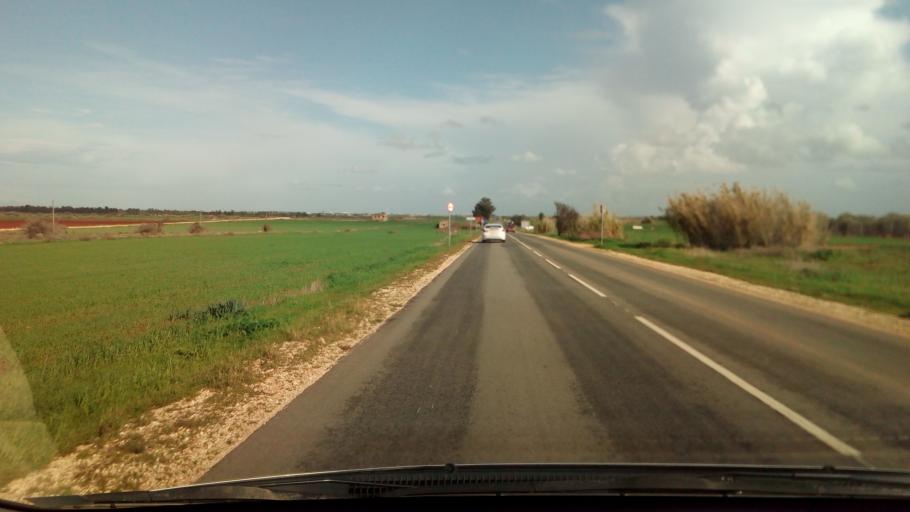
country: CY
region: Ammochostos
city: Achna
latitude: 35.0607
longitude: 33.7998
